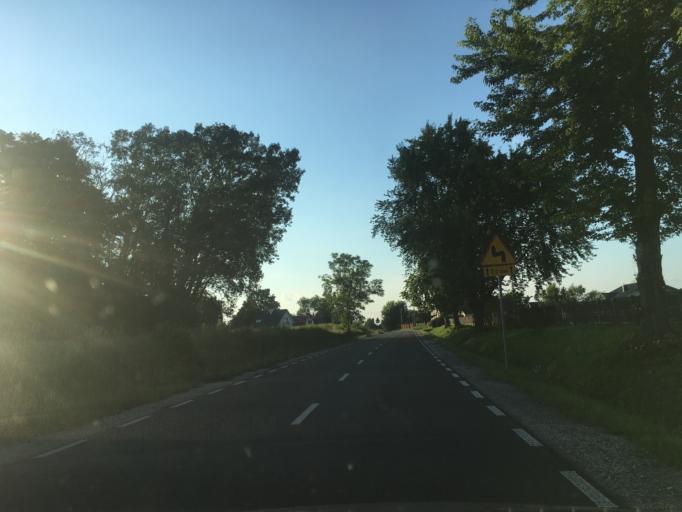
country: PL
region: Masovian Voivodeship
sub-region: Powiat warszawski zachodni
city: Bieniewice
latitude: 52.1214
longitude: 20.5663
